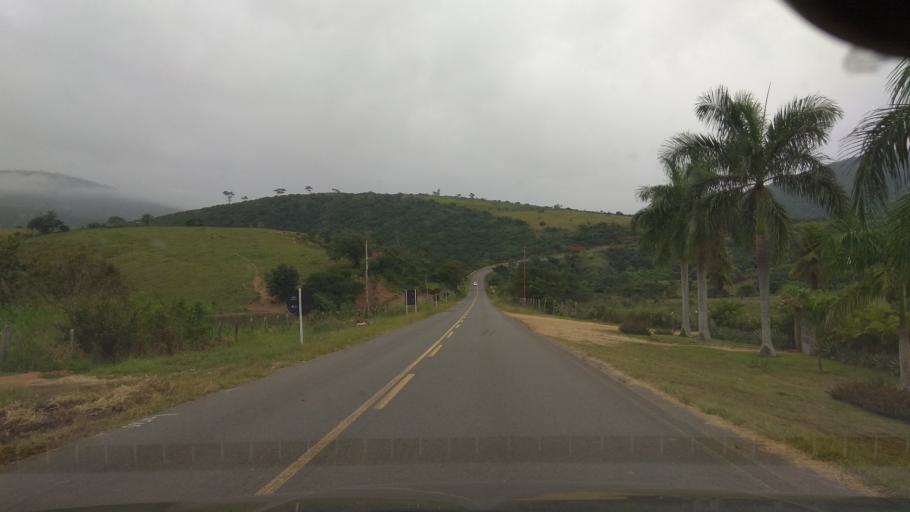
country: BR
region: Bahia
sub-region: Santa Ines
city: Santa Ines
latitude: -13.2414
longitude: -39.7542
